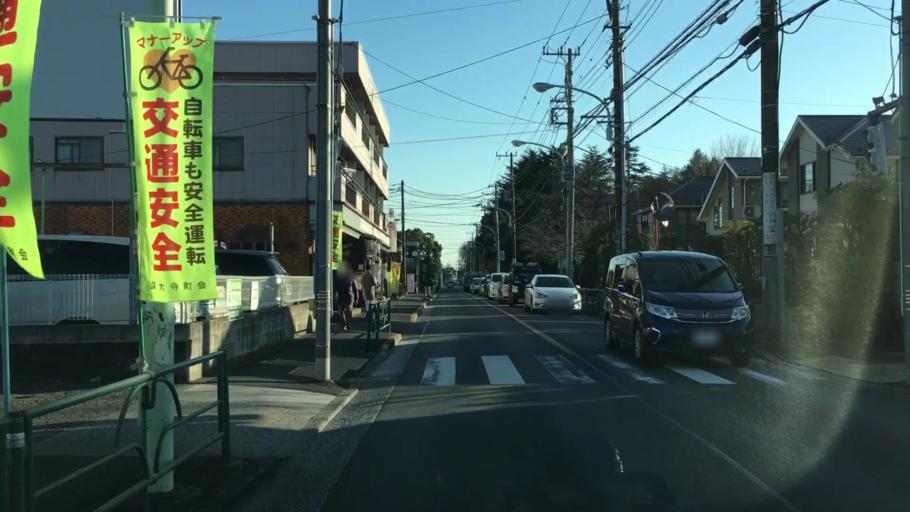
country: JP
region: Tokyo
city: Kamirenjaku
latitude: 35.6887
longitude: 139.5381
